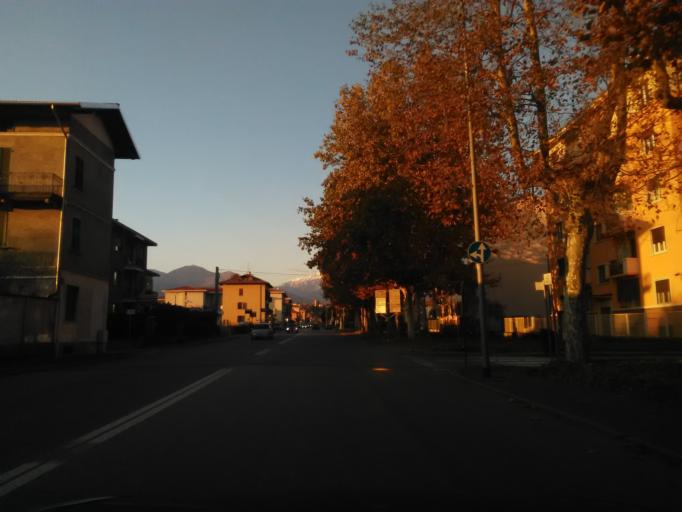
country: IT
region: Piedmont
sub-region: Provincia di Biella
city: Ponderano
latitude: 45.5462
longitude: 8.0520
